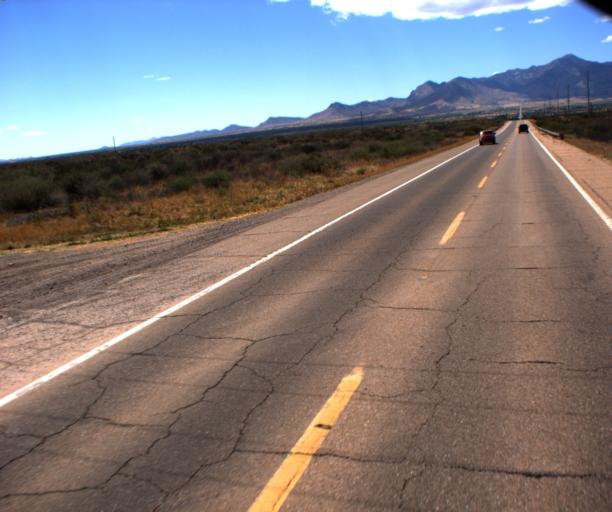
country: US
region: Arizona
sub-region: Cochise County
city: Naco
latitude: 31.3800
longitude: -110.0884
